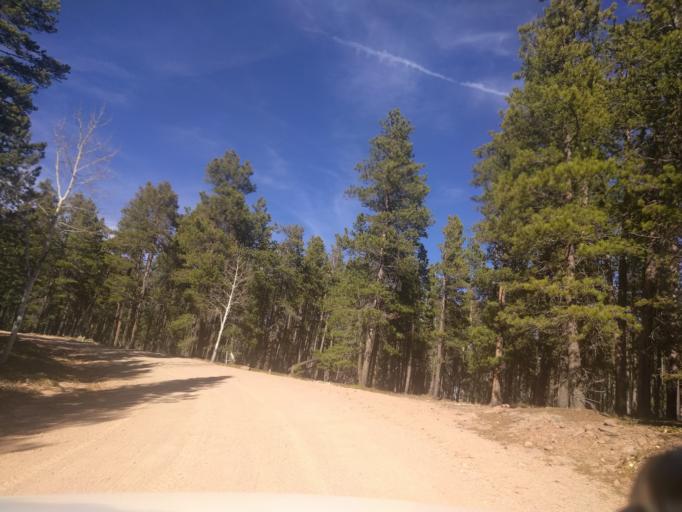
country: US
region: Colorado
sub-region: Douglas County
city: Perry Park
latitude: 39.1863
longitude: -105.0465
